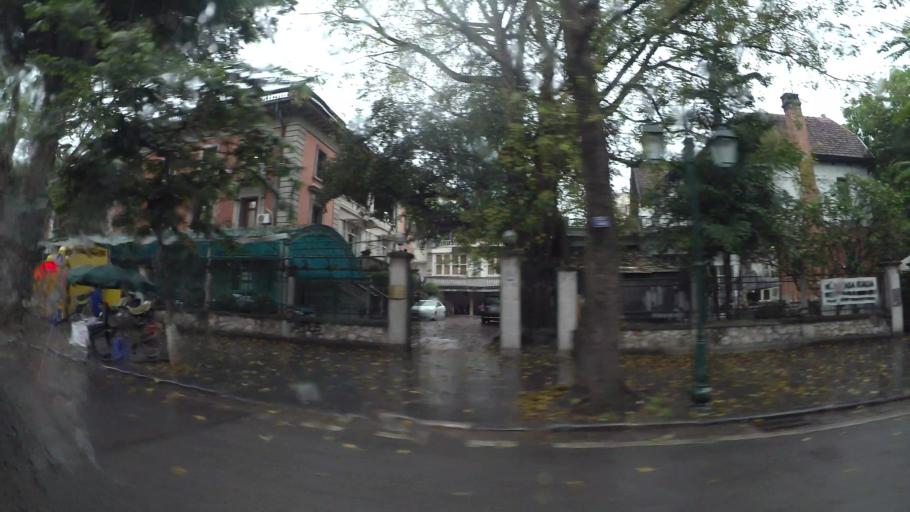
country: VN
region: Ha Noi
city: Hoan Kiem
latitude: 21.0262
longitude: 105.8566
